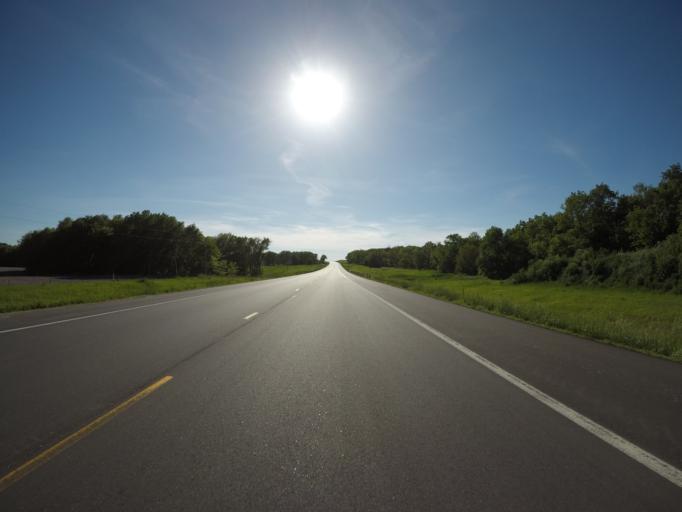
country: US
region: Kansas
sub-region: Clay County
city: Clay Center
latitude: 39.3795
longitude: -96.9713
